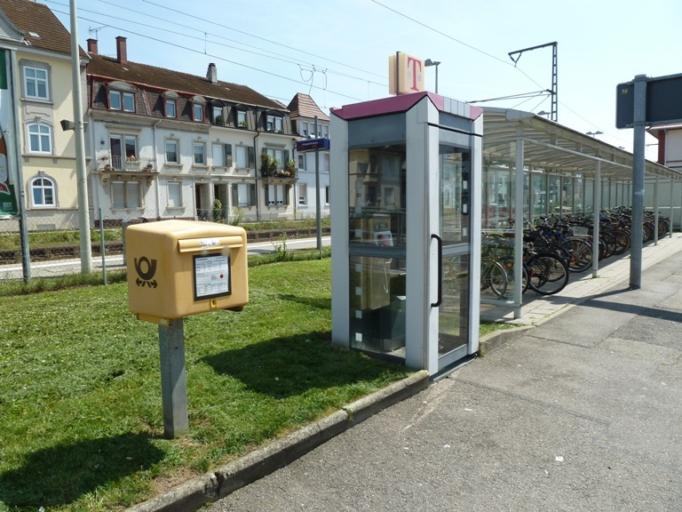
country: DE
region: Baden-Wuerttemberg
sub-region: Freiburg Region
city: Loerrach
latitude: 47.6016
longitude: 7.6590
